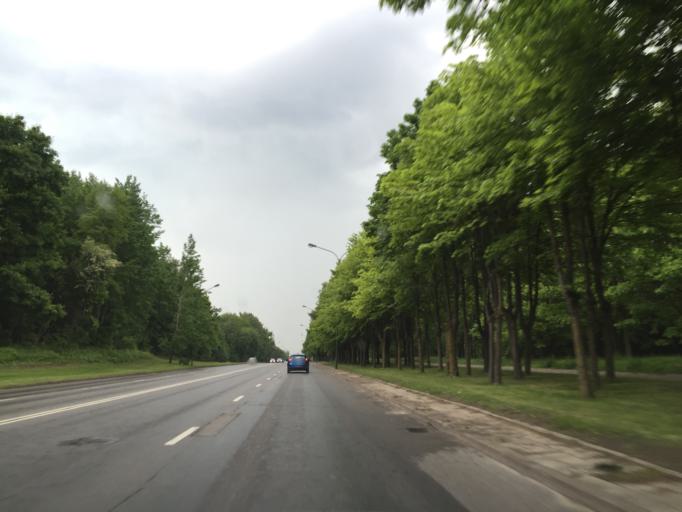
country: LT
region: Klaipedos apskritis
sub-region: Klaipeda
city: Klaipeda
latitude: 55.7385
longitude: 21.1299
